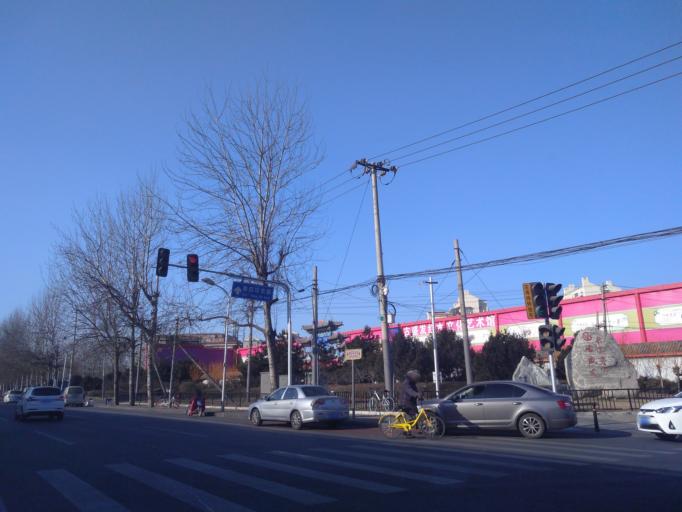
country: CN
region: Beijing
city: Jiugong
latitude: 39.8371
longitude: 116.4659
